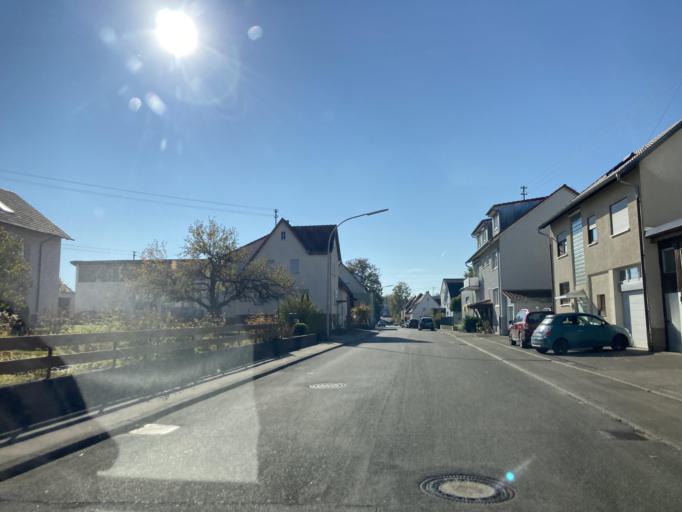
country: DE
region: Baden-Wuerttemberg
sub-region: Tuebingen Region
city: Ofterdingen
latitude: 48.4170
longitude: 9.0349
